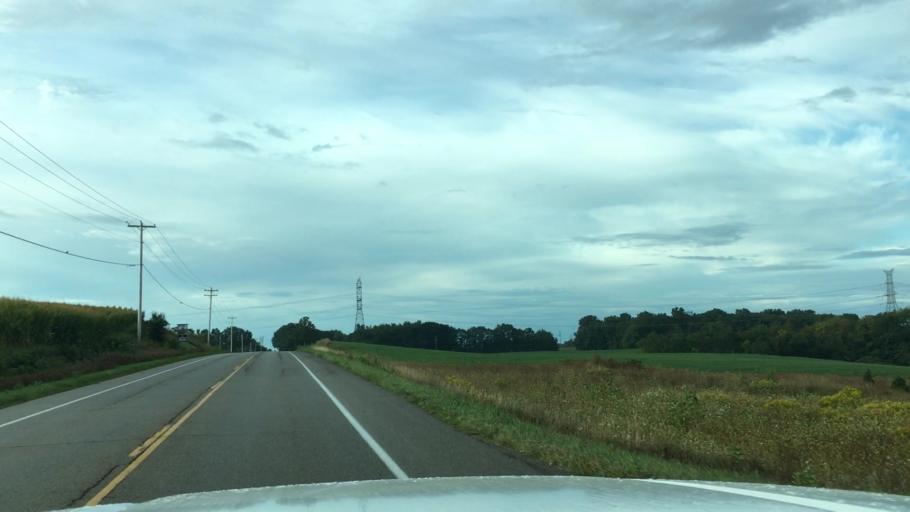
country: US
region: Michigan
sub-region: Ottawa County
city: Hudsonville
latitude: 42.7650
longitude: -85.8413
